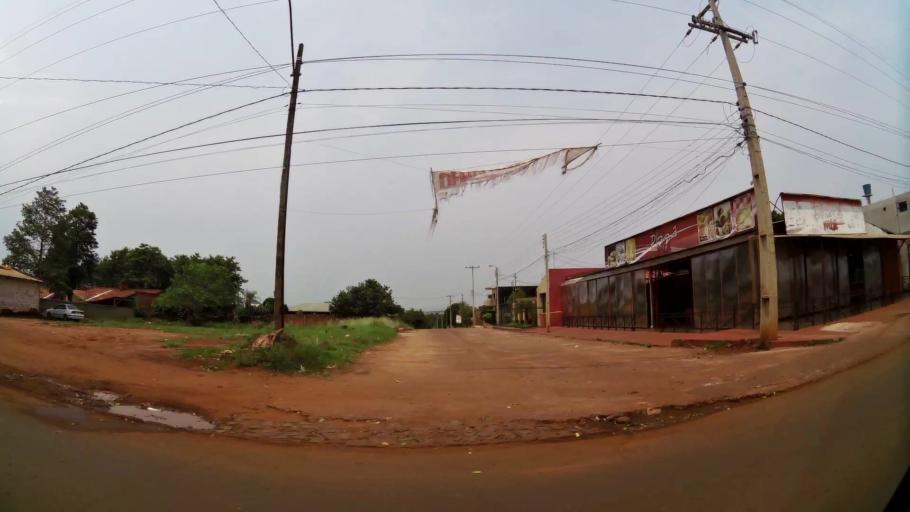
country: PY
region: Alto Parana
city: Presidente Franco
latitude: -25.5530
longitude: -54.6363
